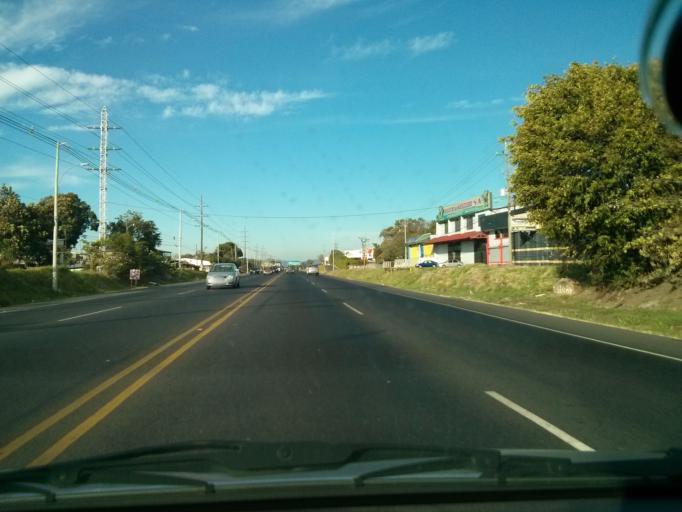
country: CR
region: Alajuela
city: Alajuela
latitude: 9.9941
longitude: -84.2391
